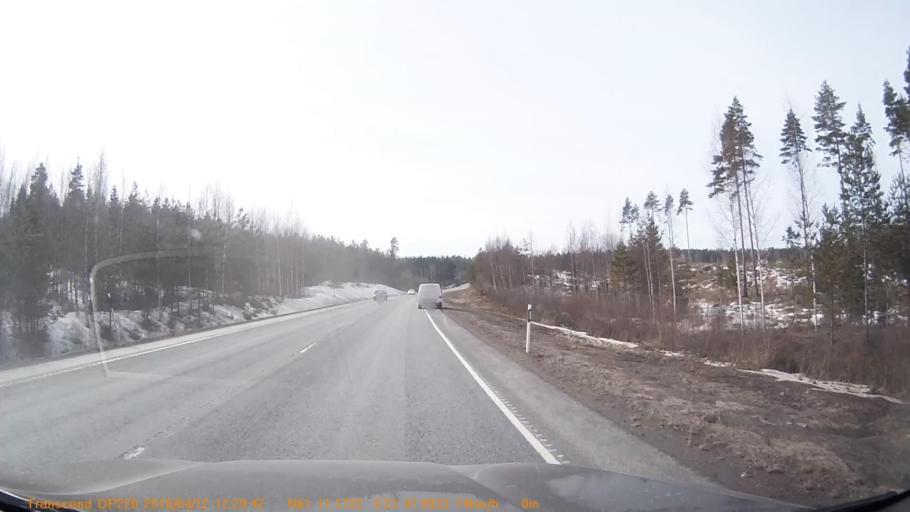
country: FI
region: Pirkanmaa
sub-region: Etelae-Pirkanmaa
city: Viiala
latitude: 61.1861
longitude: 23.7996
